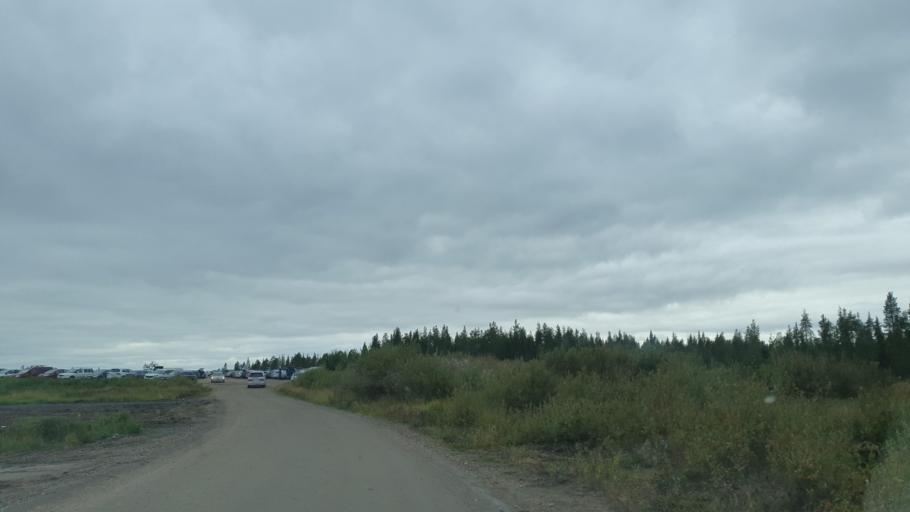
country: FI
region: Lapland
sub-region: Rovaniemi
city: Rovaniemi
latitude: 66.5033
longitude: 25.6266
